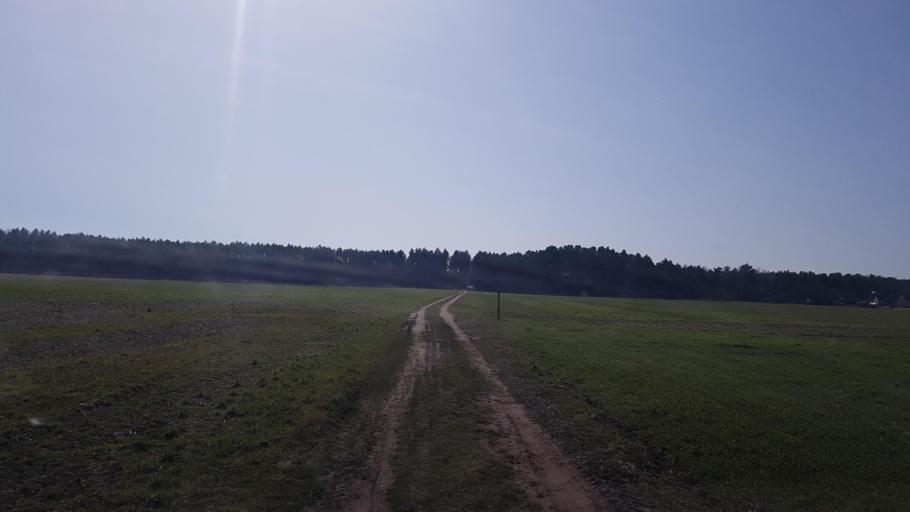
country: DE
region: Brandenburg
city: Schonewalde
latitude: 51.6399
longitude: 13.6235
